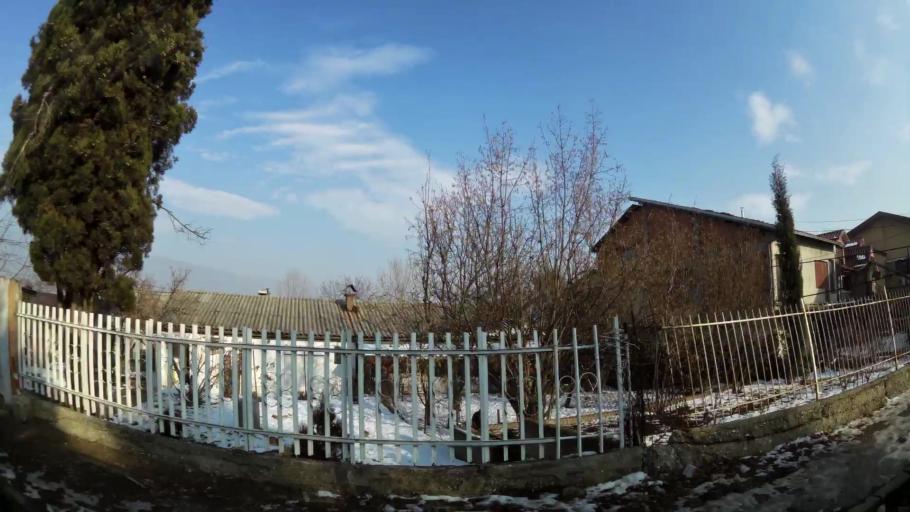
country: MK
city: Creshevo
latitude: 42.0154
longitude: 21.5053
